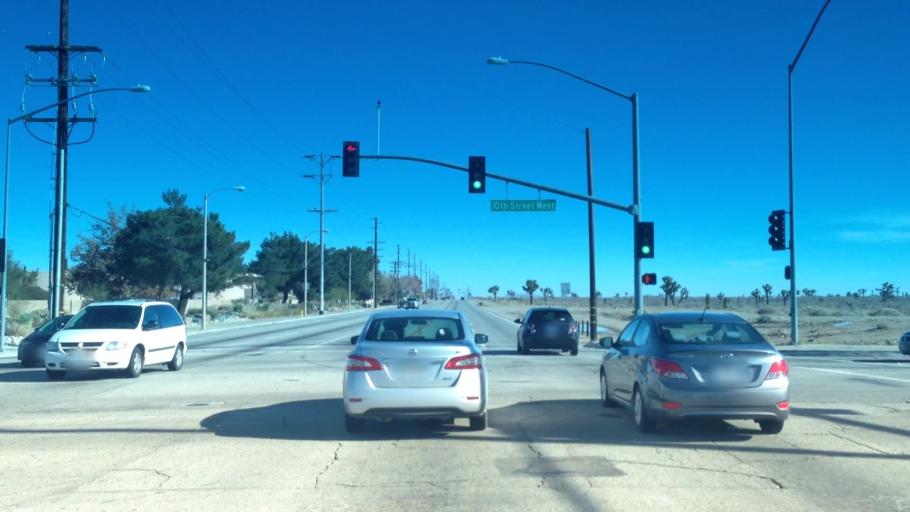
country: US
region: California
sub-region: Los Angeles County
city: Lancaster
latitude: 34.6458
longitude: -118.1478
